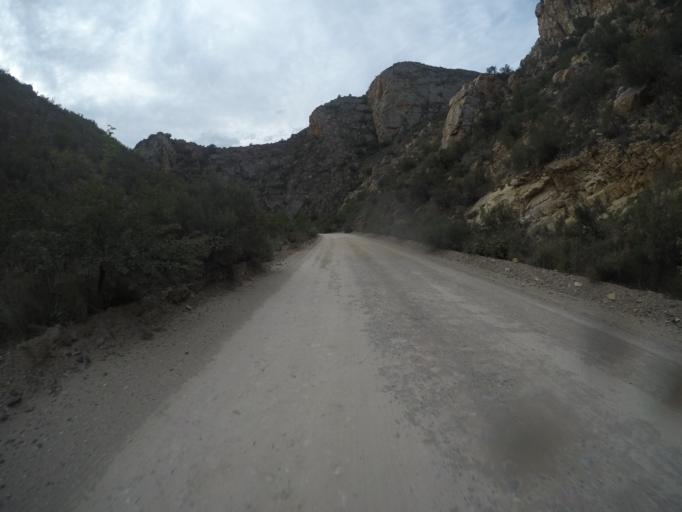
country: ZA
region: Eastern Cape
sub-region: Cacadu District Municipality
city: Willowmore
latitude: -33.5100
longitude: 23.6391
